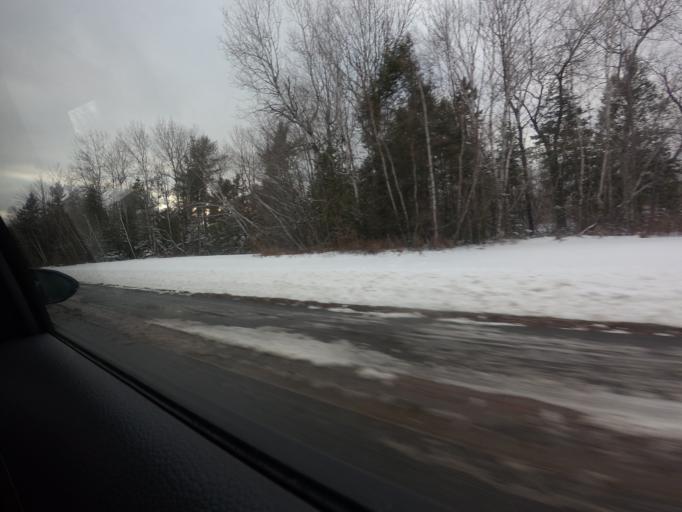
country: CA
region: New Brunswick
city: Oromocto
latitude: 45.8425
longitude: -66.4912
